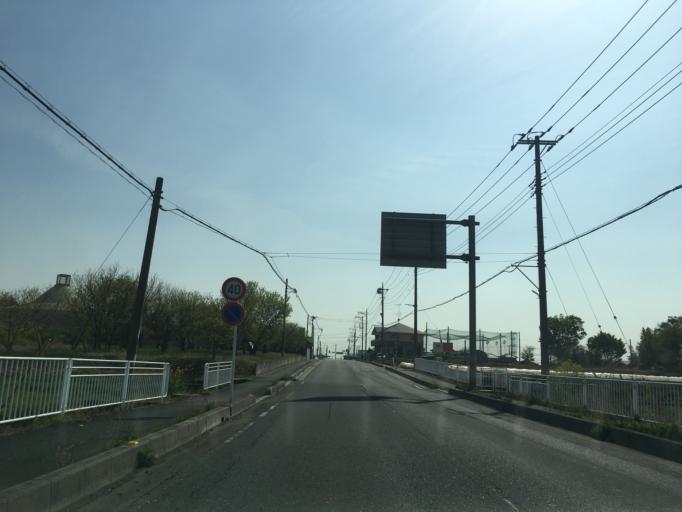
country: JP
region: Saitama
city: Sugito
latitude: 36.0136
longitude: 139.7248
